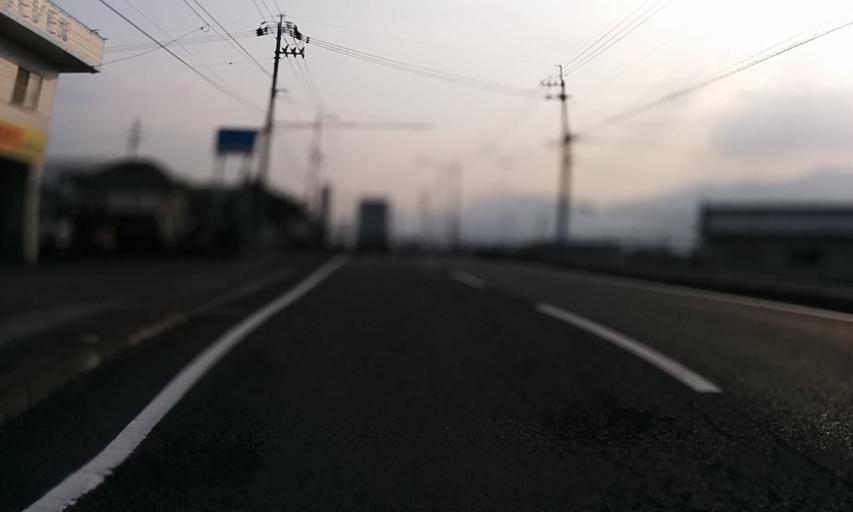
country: JP
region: Ehime
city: Saijo
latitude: 33.8948
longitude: 133.0955
